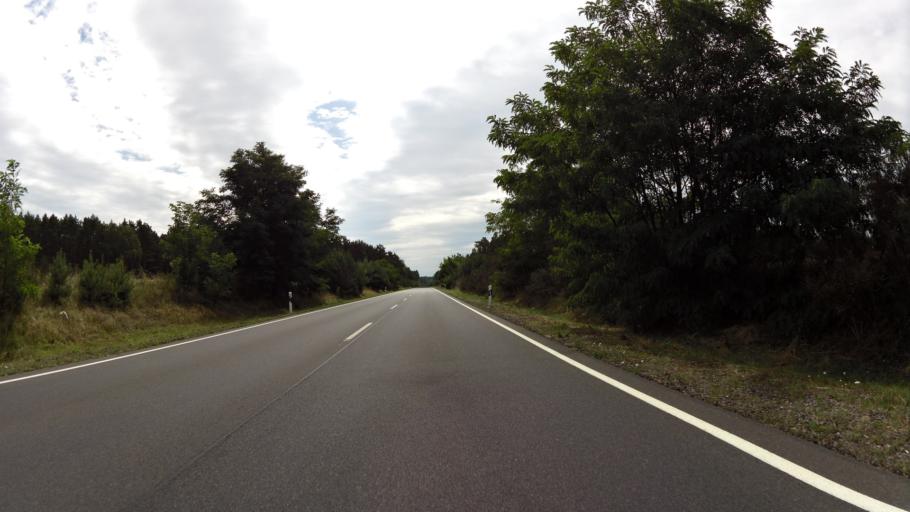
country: DE
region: Brandenburg
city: Schenkendobern
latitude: 51.9921
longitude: 14.6593
